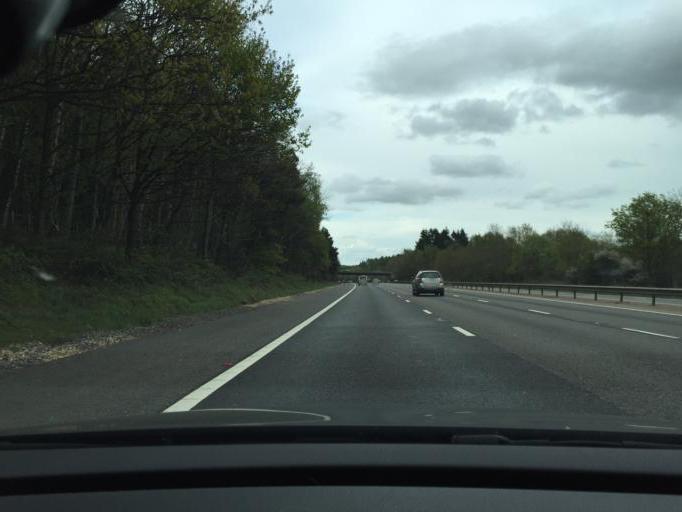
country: GB
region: England
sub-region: West Berkshire
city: Hermitage
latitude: 51.4637
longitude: -1.2550
